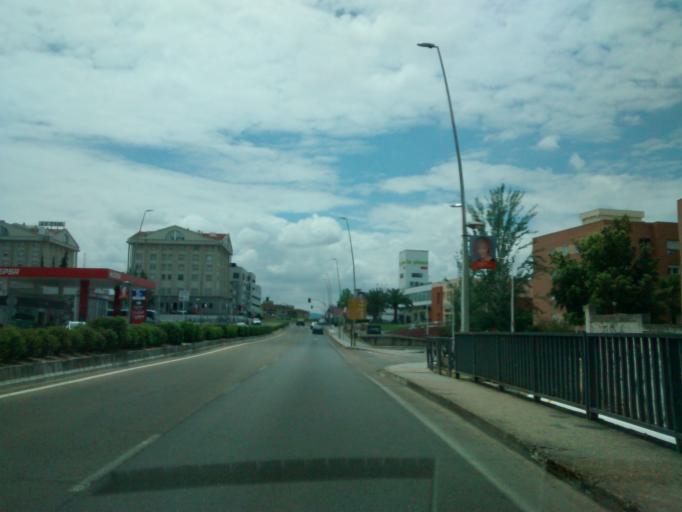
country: ES
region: Extremadura
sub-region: Provincia de Badajoz
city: Merida
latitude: 38.9159
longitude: -6.3316
